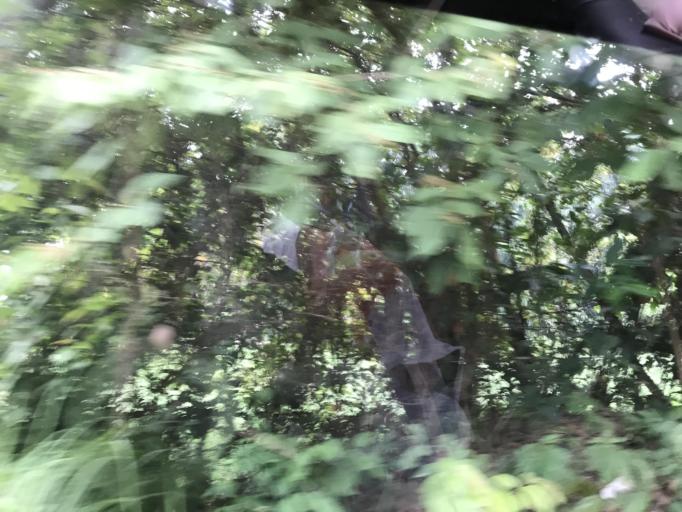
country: MY
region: Kelantan
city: Tumpat
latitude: 6.1666
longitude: 102.2004
